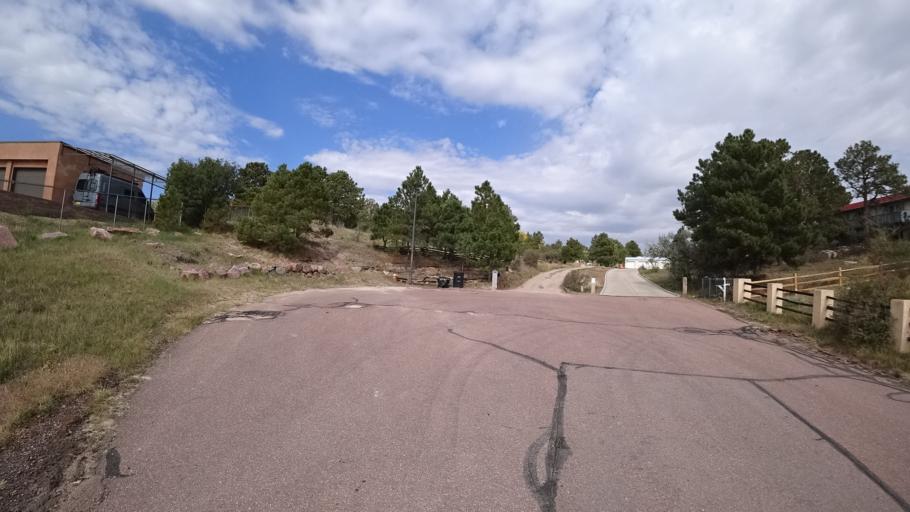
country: US
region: Colorado
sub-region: El Paso County
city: Cimarron Hills
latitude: 38.8509
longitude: -104.7239
